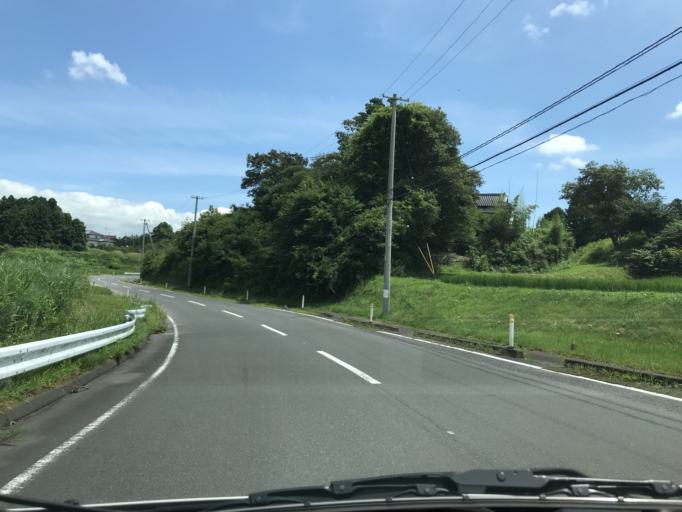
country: JP
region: Miyagi
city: Wakuya
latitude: 38.6750
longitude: 141.1075
